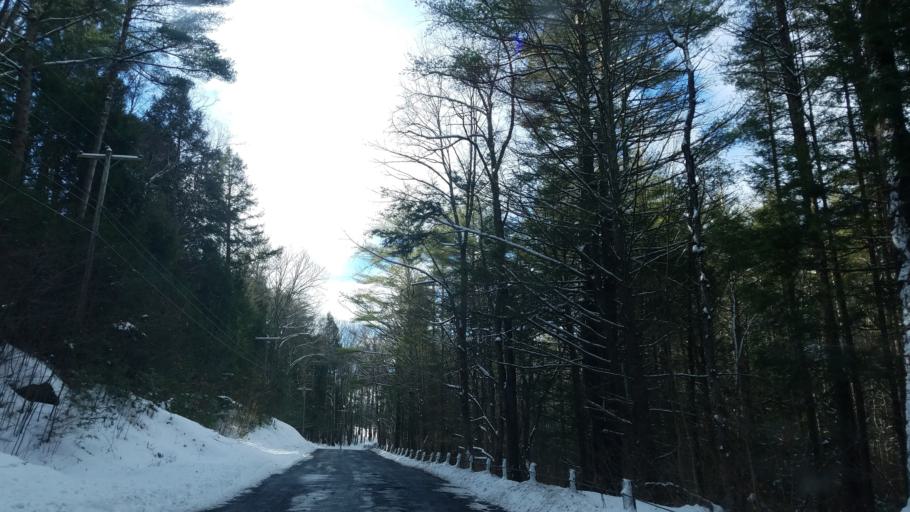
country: US
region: Connecticut
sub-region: Litchfield County
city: Winsted
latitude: 41.9683
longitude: -73.0444
